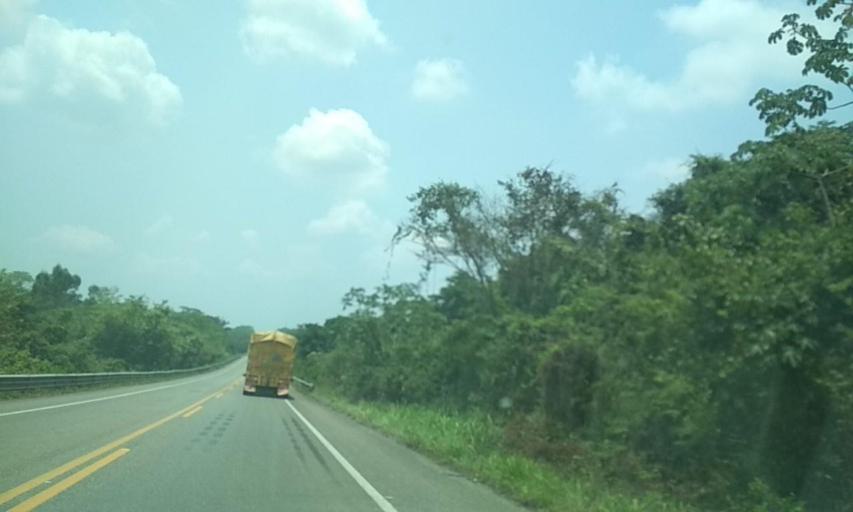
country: MX
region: Tabasco
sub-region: Huimanguillo
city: Francisco Rueda
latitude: 17.7337
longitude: -93.9720
